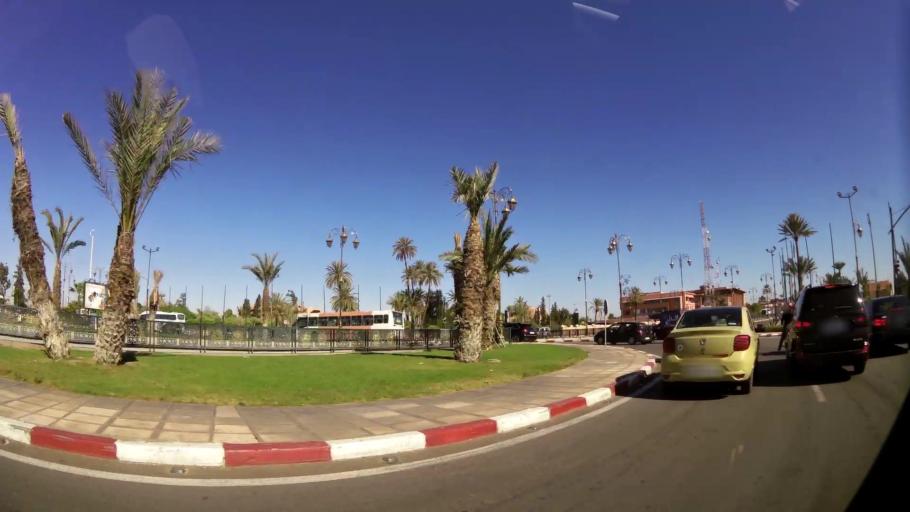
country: MA
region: Marrakech-Tensift-Al Haouz
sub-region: Marrakech
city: Marrakesh
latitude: 31.6446
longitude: -7.9872
